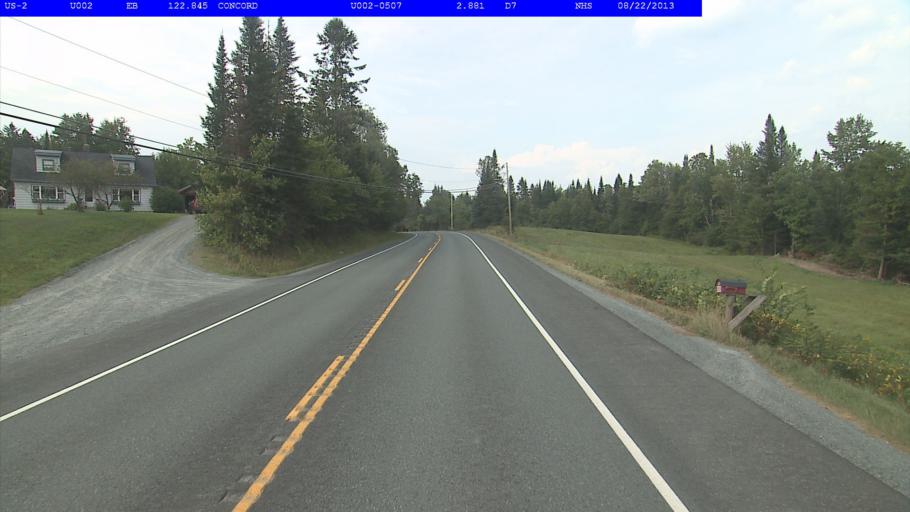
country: US
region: Vermont
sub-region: Caledonia County
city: St Johnsbury
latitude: 44.4359
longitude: -71.8790
